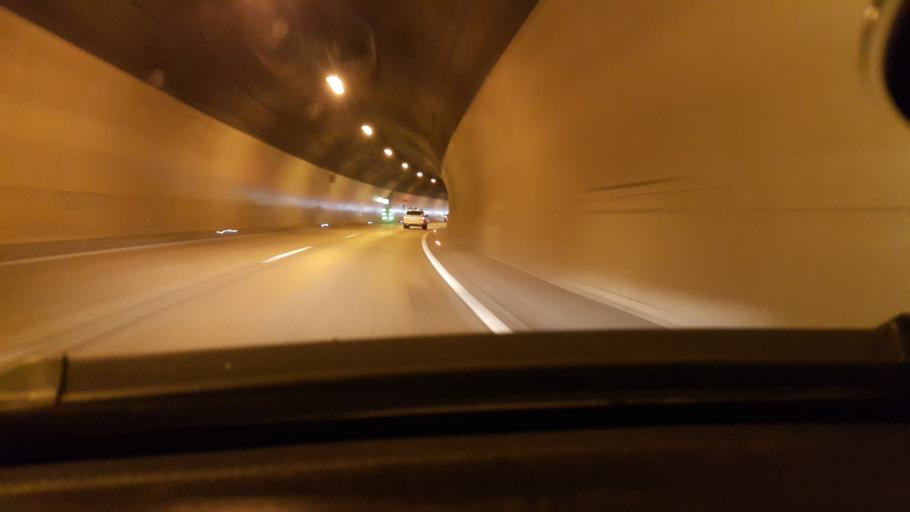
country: AT
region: Styria
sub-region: Politischer Bezirk Voitsberg
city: Modriach
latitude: 46.9646
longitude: 15.0663
